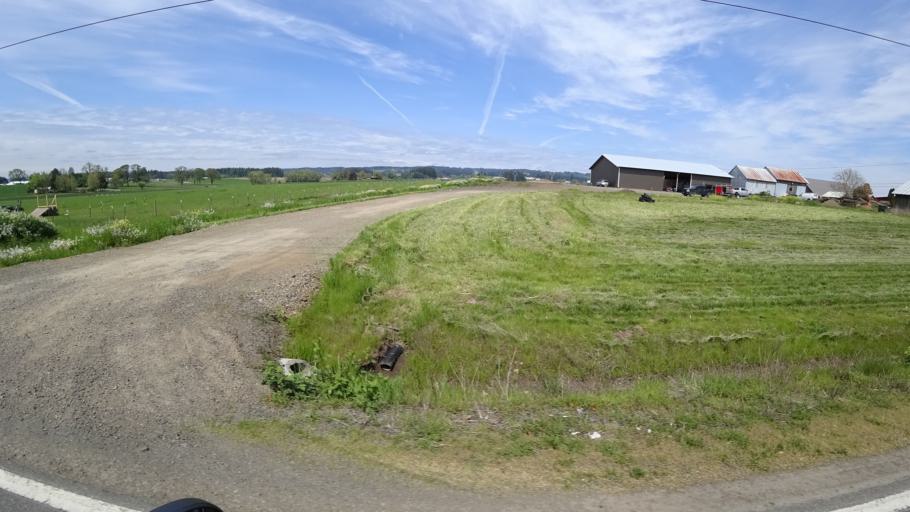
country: US
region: Oregon
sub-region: Washington County
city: Rockcreek
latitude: 45.5757
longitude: -122.9162
